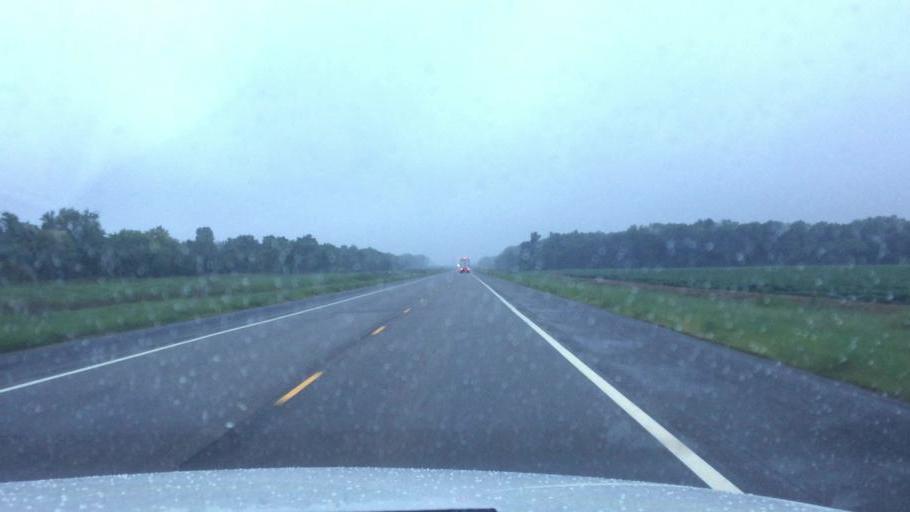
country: US
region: Kansas
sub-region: Montgomery County
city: Cherryvale
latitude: 37.4200
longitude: -95.4951
